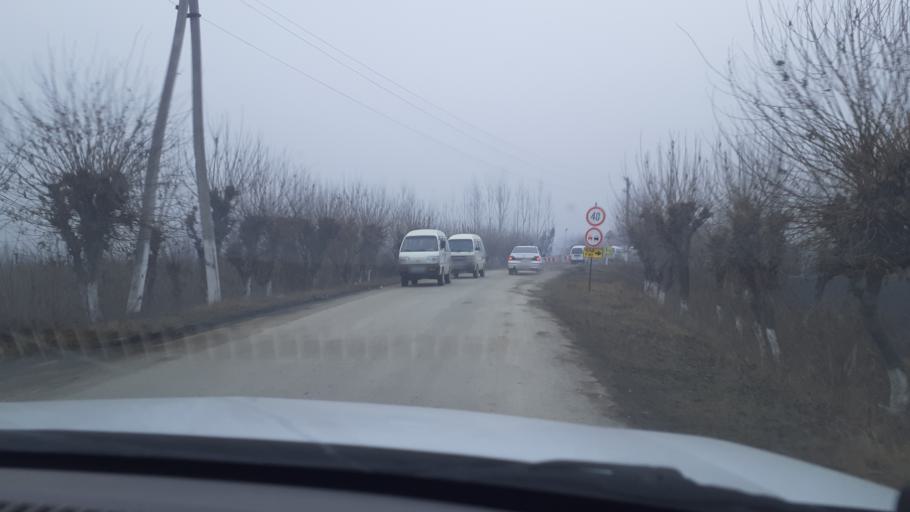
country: UZ
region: Namangan
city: Haqqulobod
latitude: 40.9010
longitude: 71.9966
